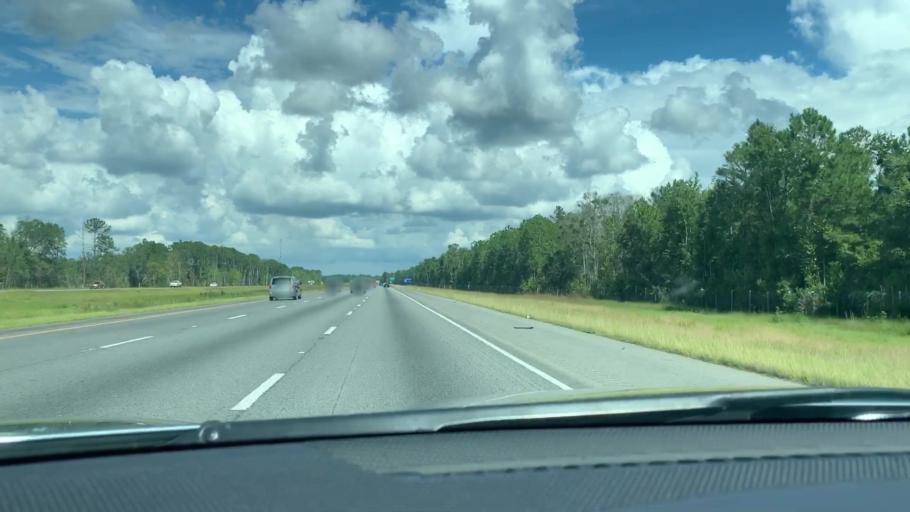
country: US
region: Georgia
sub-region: Glynn County
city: Brunswick
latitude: 31.0794
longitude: -81.6158
